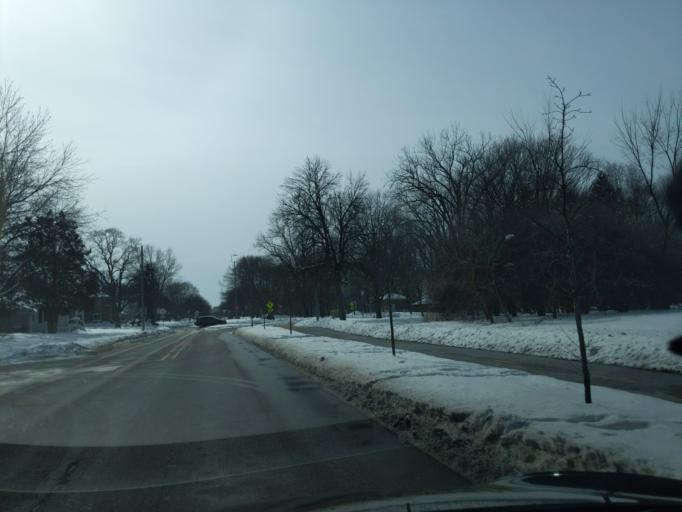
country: US
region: Michigan
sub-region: Kent County
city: Comstock Park
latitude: 43.0072
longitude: -85.6680
